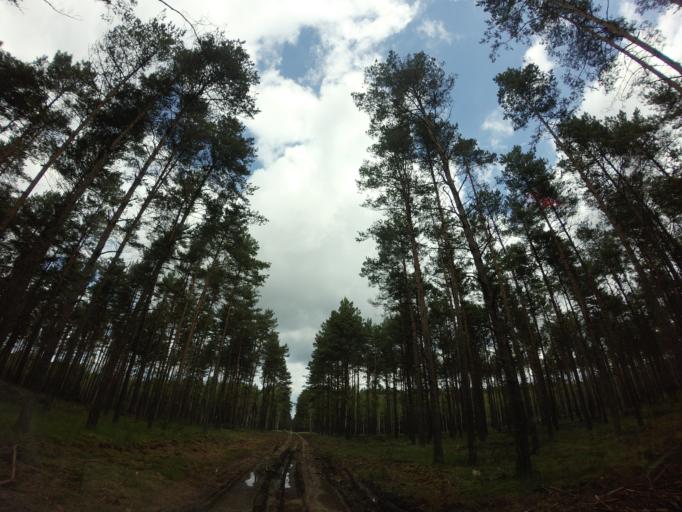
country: PL
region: West Pomeranian Voivodeship
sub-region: Powiat drawski
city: Kalisz Pomorski
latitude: 53.1855
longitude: 15.8989
